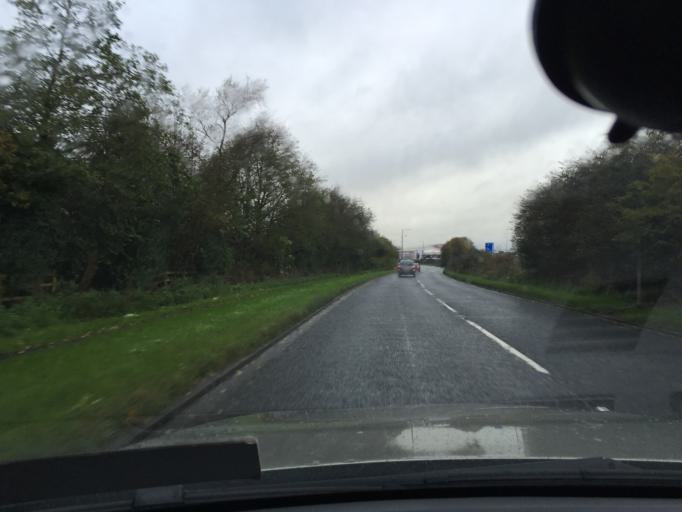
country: GB
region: Northern Ireland
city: Carnmoney
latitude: 54.6704
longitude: -5.9697
